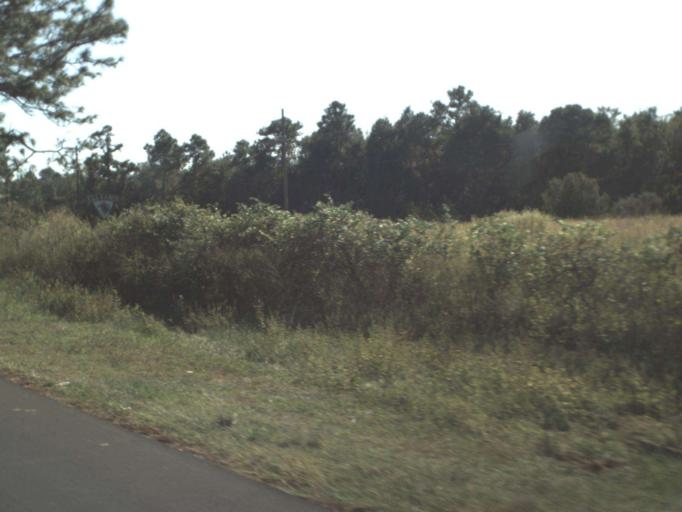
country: US
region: Florida
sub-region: Walton County
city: DeFuniak Springs
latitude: 30.7496
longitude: -86.1481
